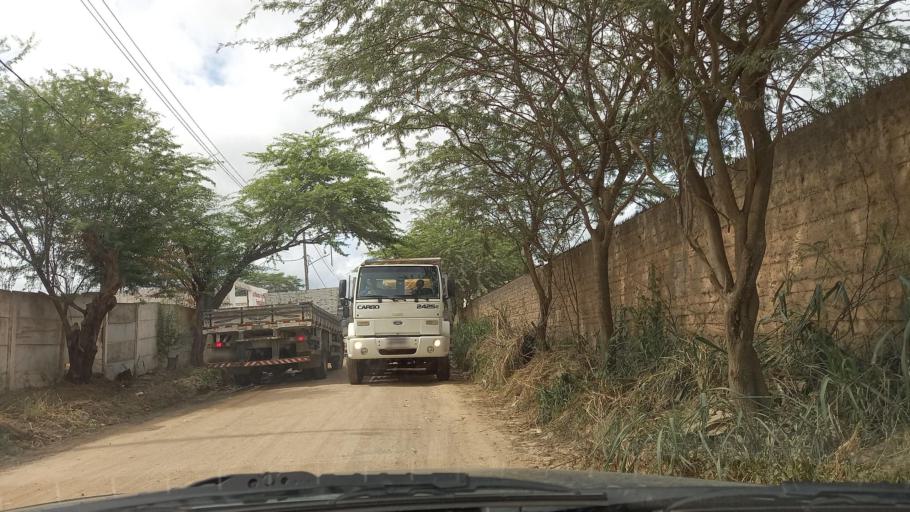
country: BR
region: Pernambuco
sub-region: Gravata
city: Gravata
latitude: -8.1948
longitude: -35.5738
